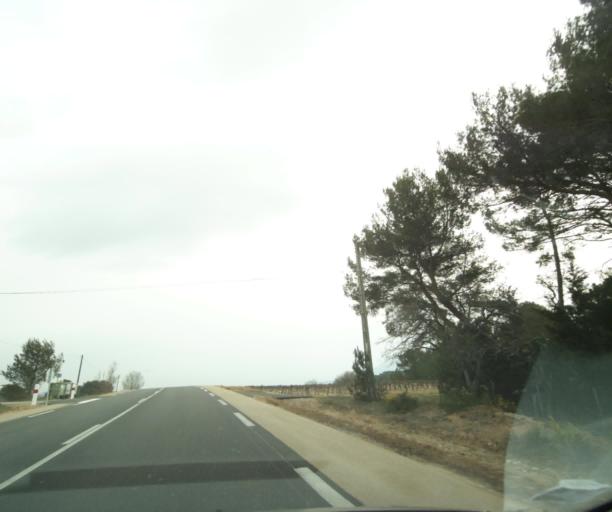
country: FR
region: Provence-Alpes-Cote d'Azur
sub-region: Departement des Bouches-du-Rhone
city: Rousset
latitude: 43.4898
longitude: 5.6467
